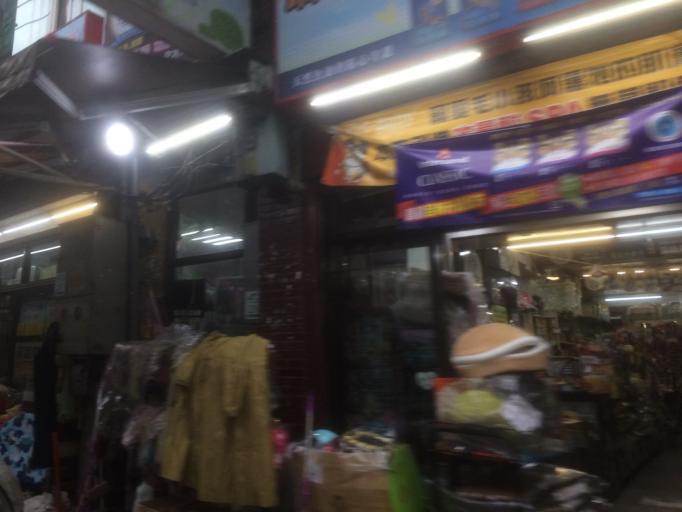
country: TW
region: Taiwan
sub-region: Yilan
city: Yilan
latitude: 24.6753
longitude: 121.7679
